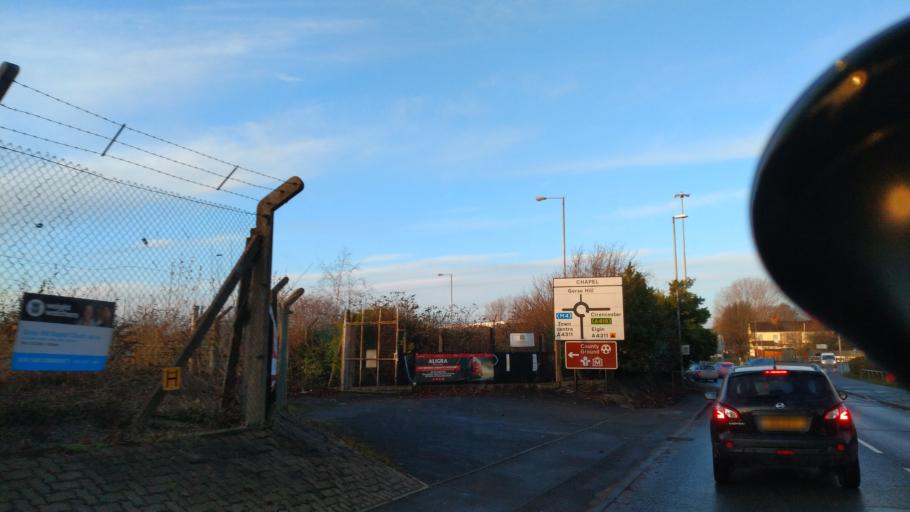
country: GB
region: England
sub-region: Borough of Swindon
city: Swindon
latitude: 51.5719
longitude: -1.7694
